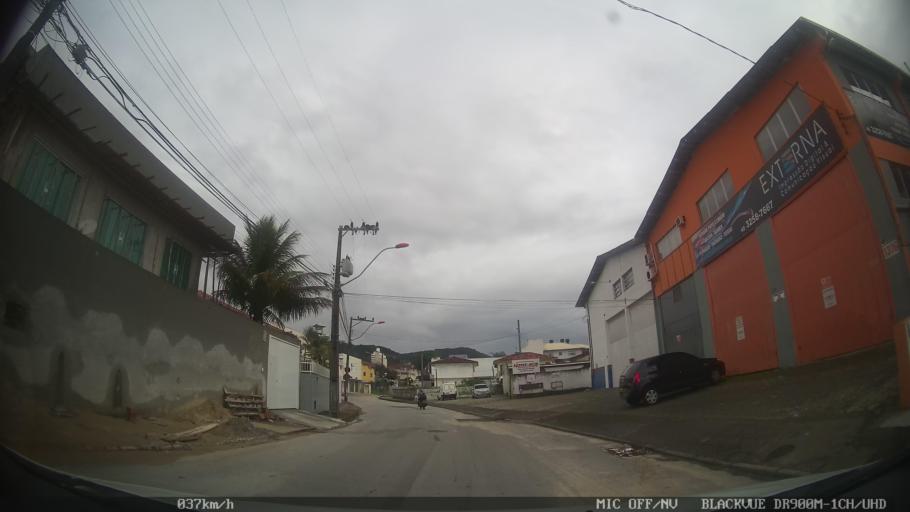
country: BR
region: Santa Catarina
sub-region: Sao Jose
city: Campinas
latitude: -27.5685
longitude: -48.6249
